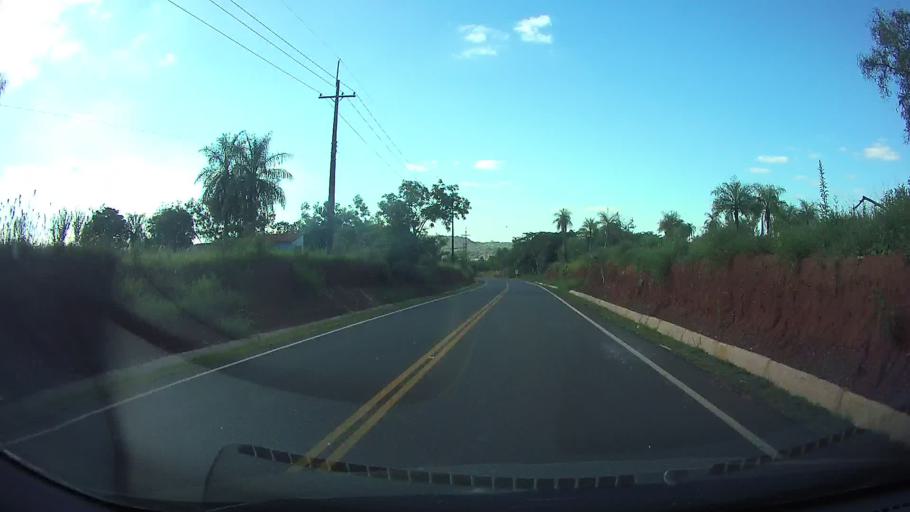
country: PY
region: Cordillera
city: Caacupe
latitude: -25.3660
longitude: -57.1450
